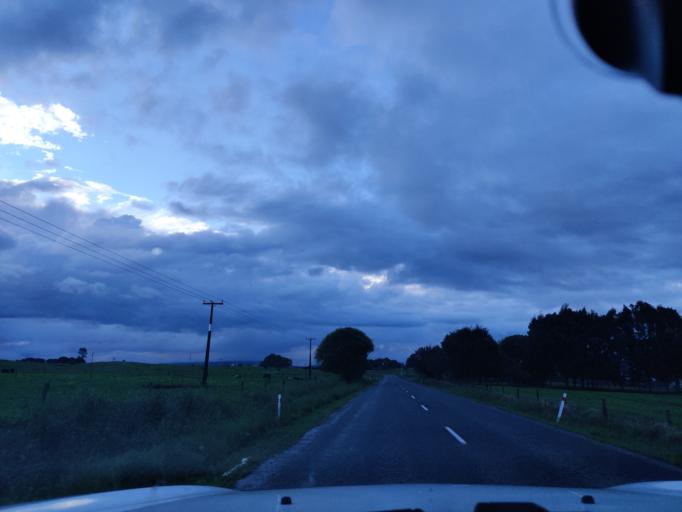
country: NZ
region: Waikato
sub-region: South Waikato District
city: Tokoroa
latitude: -38.2223
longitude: 175.8320
